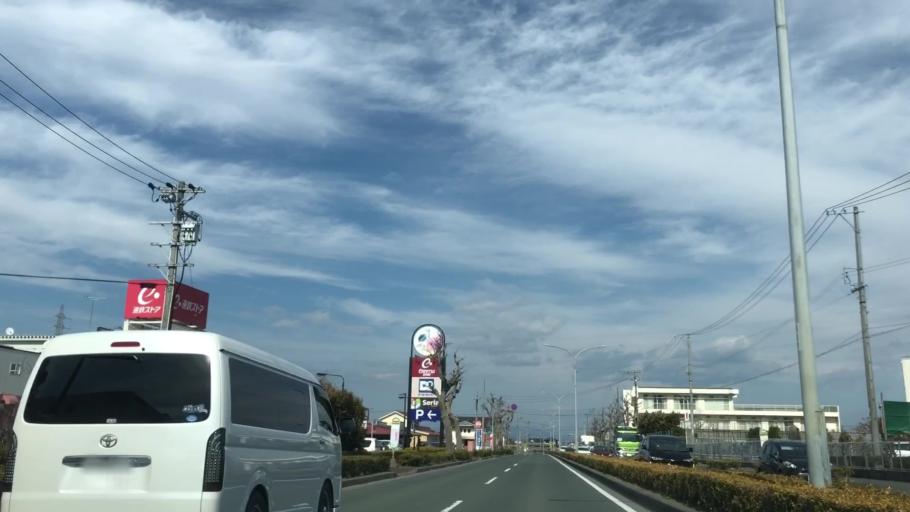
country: JP
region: Shizuoka
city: Hamamatsu
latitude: 34.7318
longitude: 137.6585
